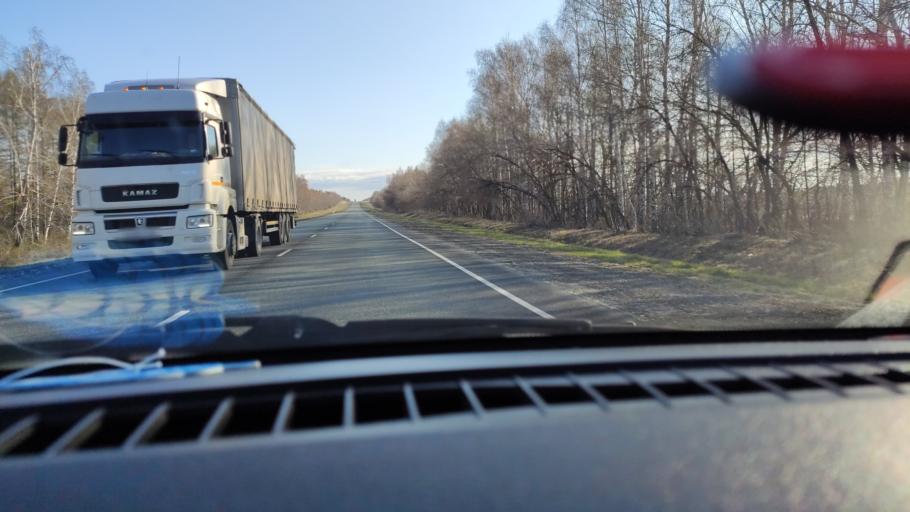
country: RU
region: Saratov
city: Khvalynsk
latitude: 52.5795
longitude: 48.1146
